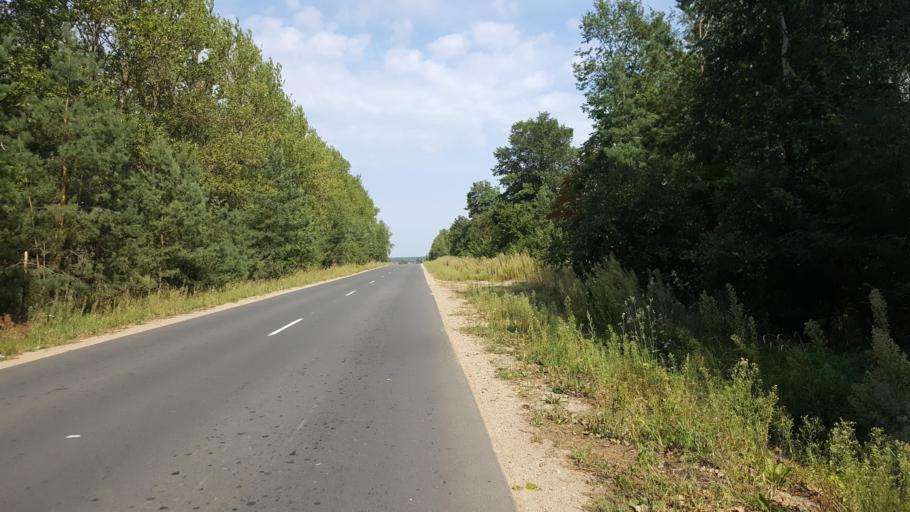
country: BY
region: Brest
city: Kamyanyets
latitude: 52.4548
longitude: 23.7358
